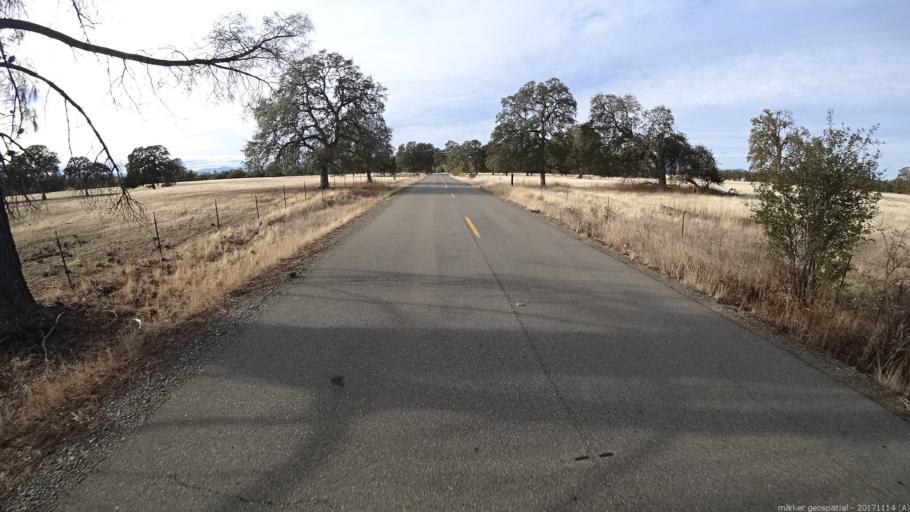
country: US
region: California
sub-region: Shasta County
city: Shasta
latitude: 40.3905
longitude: -122.4998
